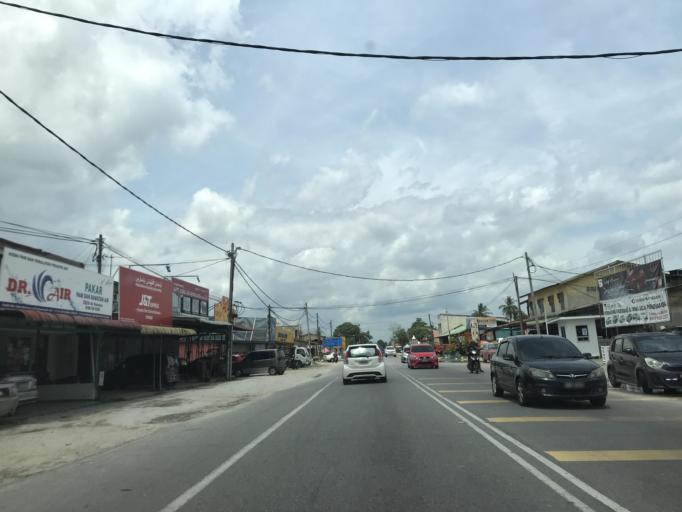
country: MY
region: Kelantan
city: Kota Bharu
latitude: 6.1103
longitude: 102.2131
